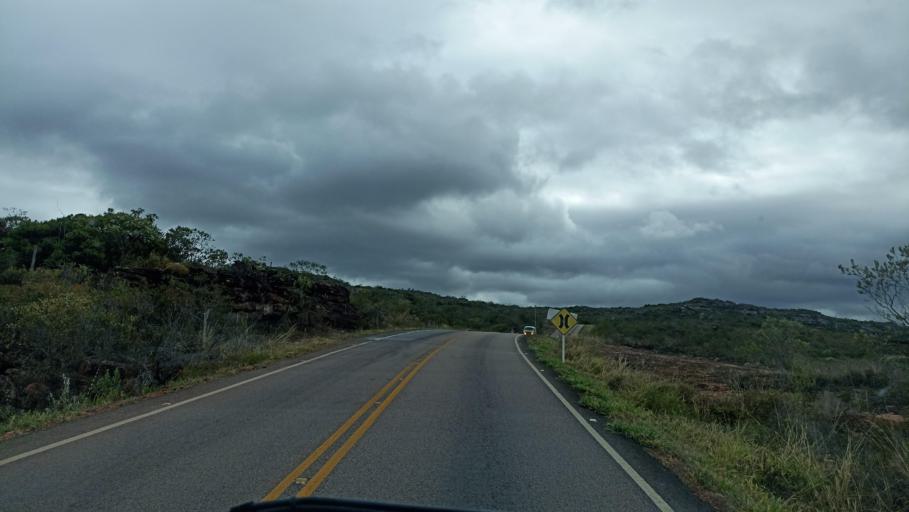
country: BR
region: Bahia
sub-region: Andarai
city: Vera Cruz
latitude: -12.9935
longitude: -41.3521
